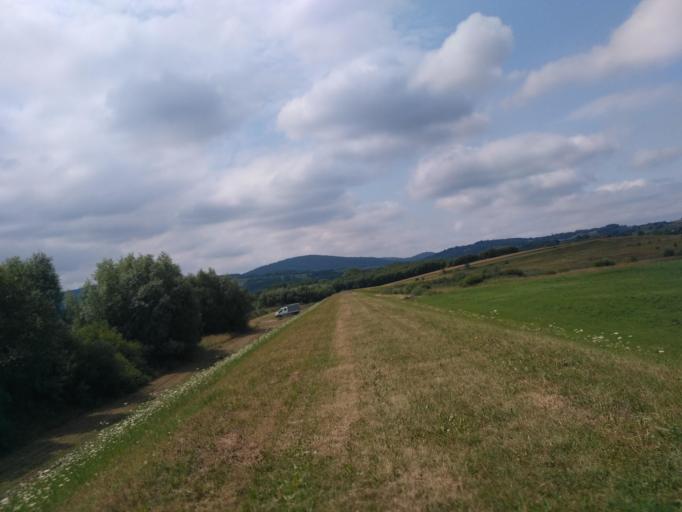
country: PL
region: Subcarpathian Voivodeship
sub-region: Powiat krosnienski
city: Rymanow
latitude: 49.5955
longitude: 21.8455
